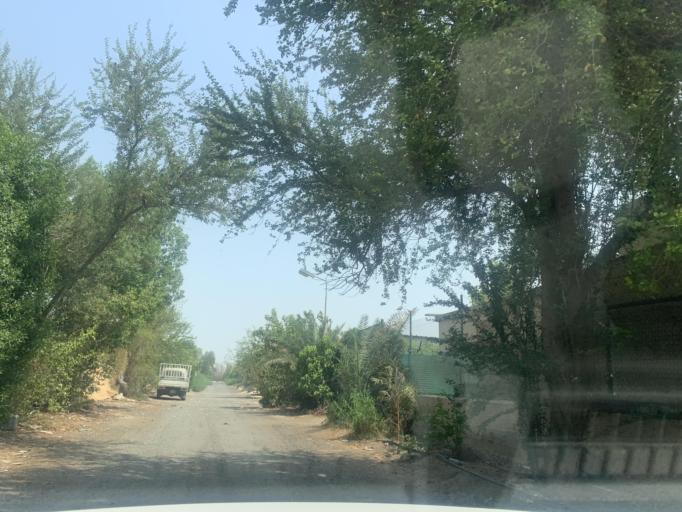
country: BH
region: Central Governorate
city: Madinat Hamad
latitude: 26.1414
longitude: 50.4774
